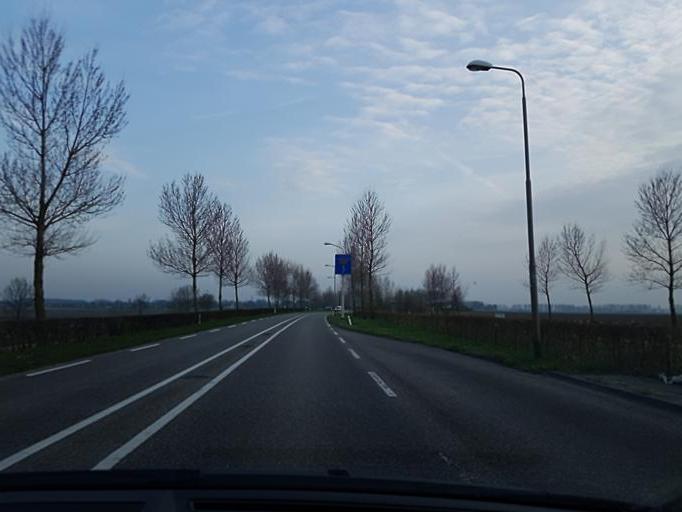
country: NL
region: Zeeland
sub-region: Gemeente Hulst
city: Hulst
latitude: 51.3038
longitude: 4.0434
